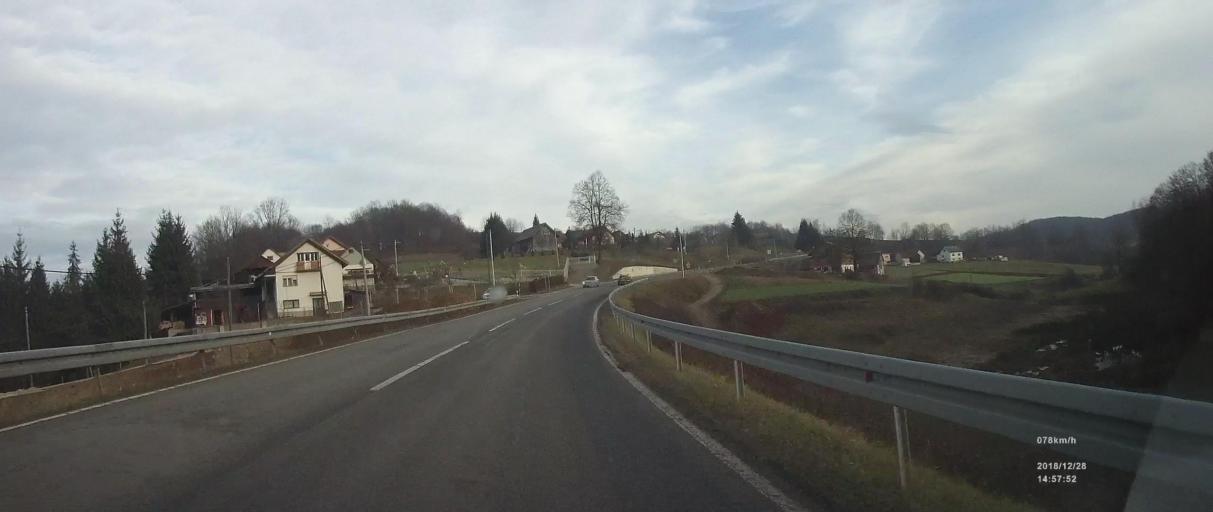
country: HR
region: Karlovacka
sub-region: Grad Karlovac
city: Karlovac
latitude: 45.4561
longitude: 15.4629
